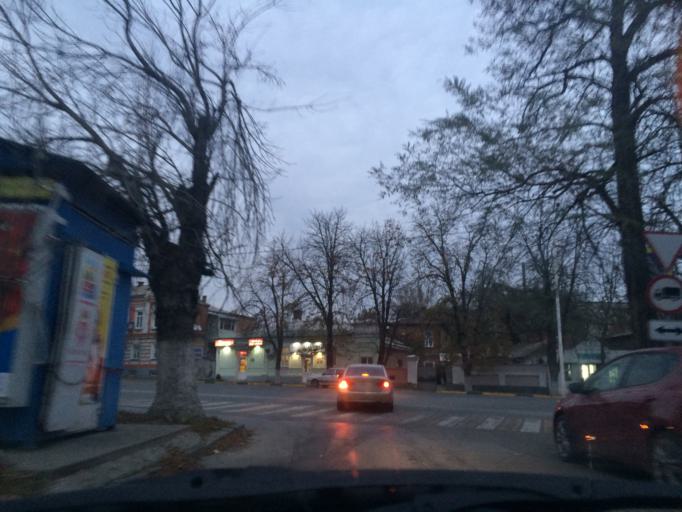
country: RU
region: Rostov
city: Novocherkassk
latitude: 47.4199
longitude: 40.0928
